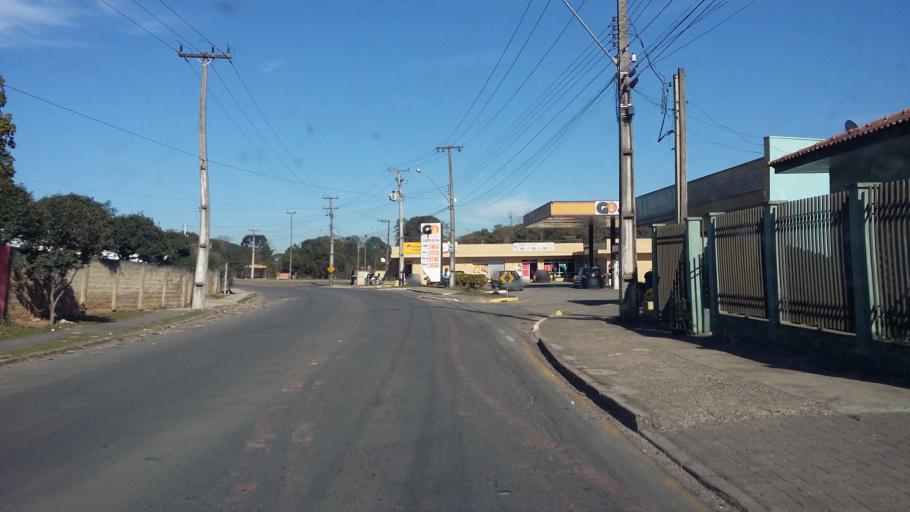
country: BR
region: Parana
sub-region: Campo Largo
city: Campo Largo
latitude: -25.4674
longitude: -49.5658
